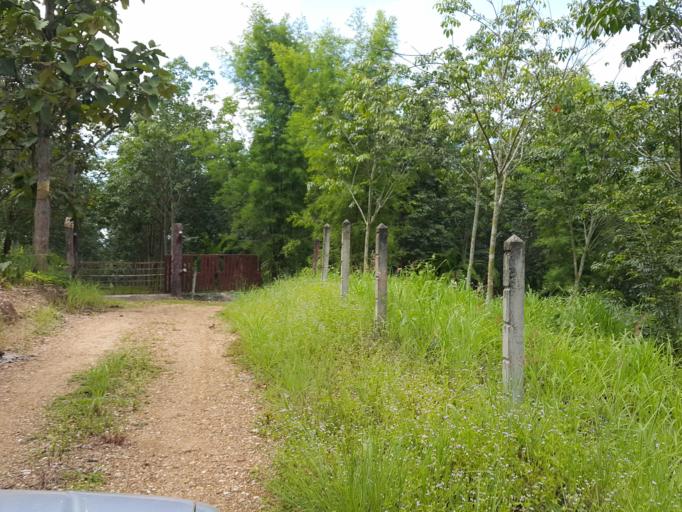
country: TH
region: Chiang Mai
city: Mae Taeng
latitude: 18.9541
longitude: 98.9113
